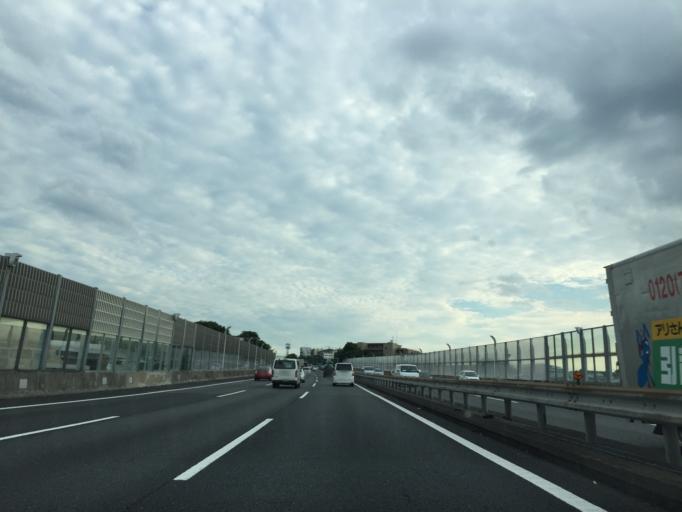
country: JP
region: Tokyo
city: Chofugaoka
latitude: 35.6107
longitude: 139.5873
